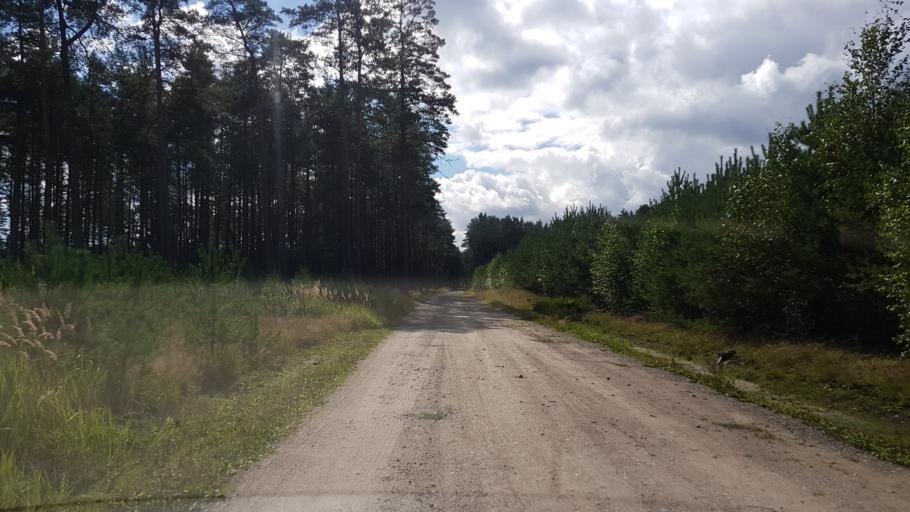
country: PL
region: West Pomeranian Voivodeship
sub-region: Powiat bialogardzki
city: Tychowo
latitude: 54.0250
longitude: 16.3001
